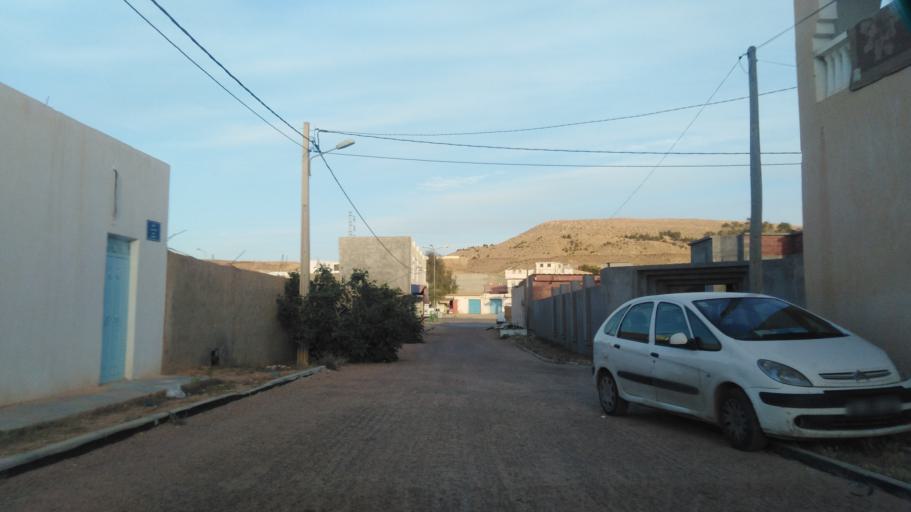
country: TN
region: Tataouine
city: Tataouine
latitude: 32.9416
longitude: 10.4596
